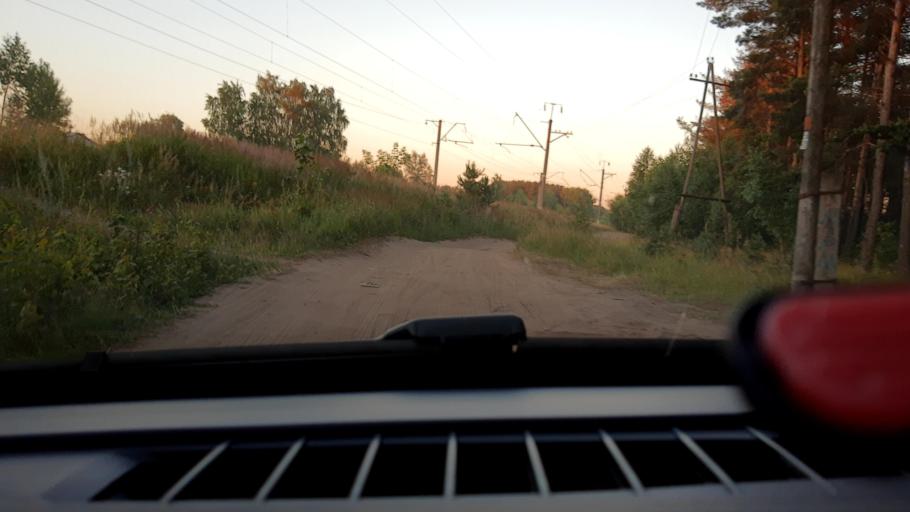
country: RU
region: Nizjnij Novgorod
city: Gorbatovka
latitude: 56.3812
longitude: 43.7727
